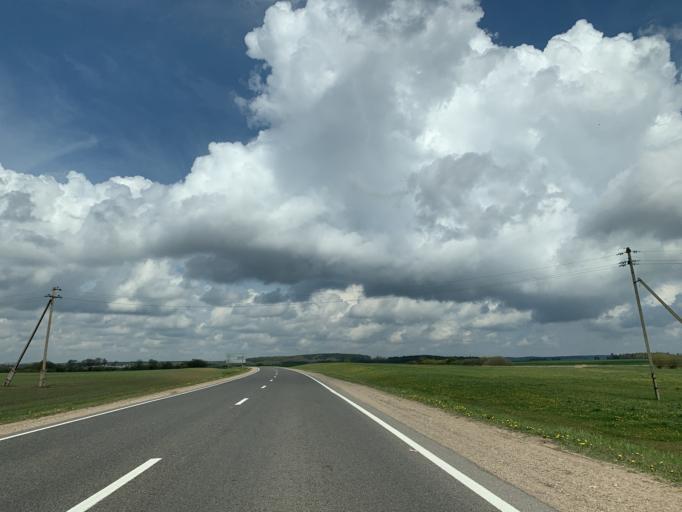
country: BY
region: Minsk
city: Nyasvizh
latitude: 53.2308
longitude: 26.7229
